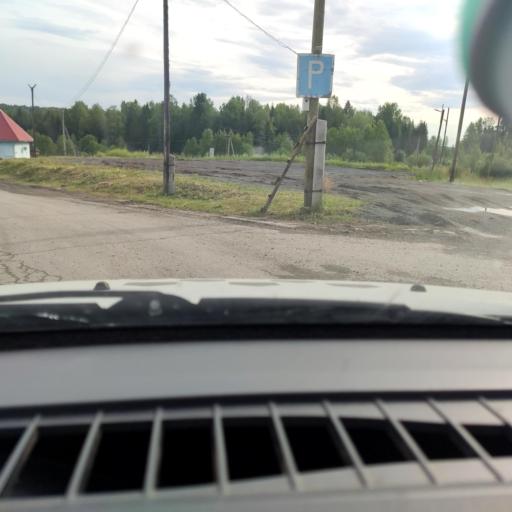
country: RU
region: Perm
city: Siva
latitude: 58.6273
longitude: 53.8705
